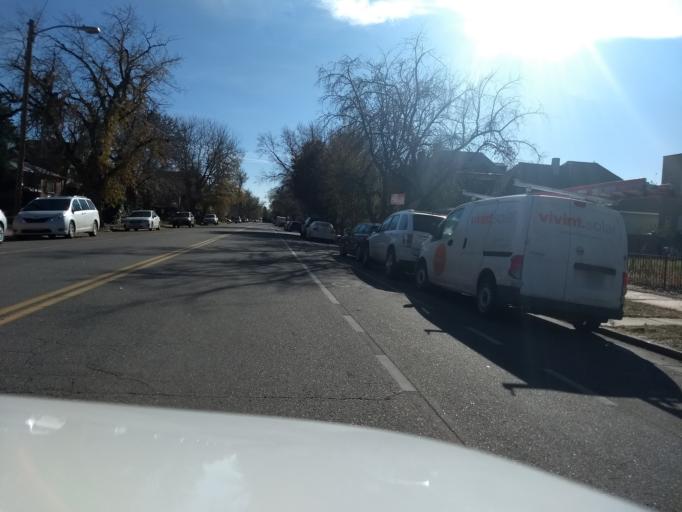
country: US
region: Colorado
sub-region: Denver County
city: Denver
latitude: 39.7208
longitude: -104.9909
